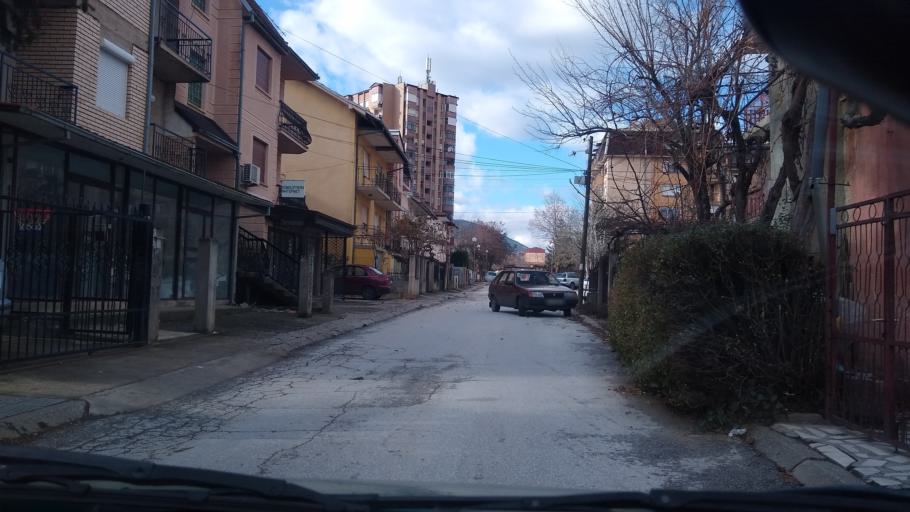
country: MK
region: Bitola
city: Bitola
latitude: 41.0260
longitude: 21.3193
